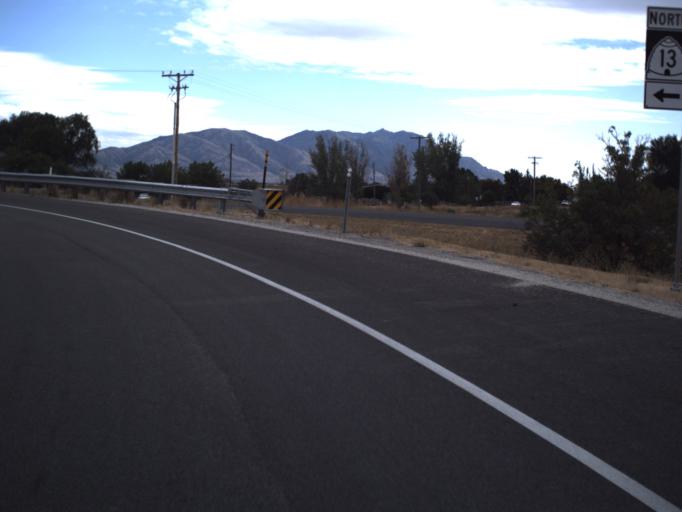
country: US
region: Utah
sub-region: Box Elder County
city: Elwood
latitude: 41.6786
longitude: -112.1424
